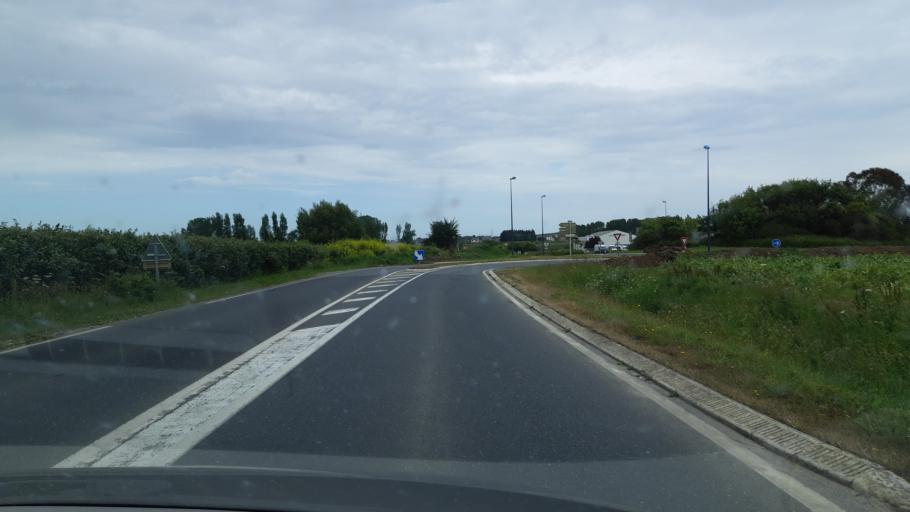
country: FR
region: Brittany
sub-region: Departement du Finistere
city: Saint-Pol-de-Leon
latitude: 48.6700
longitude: -4.0092
